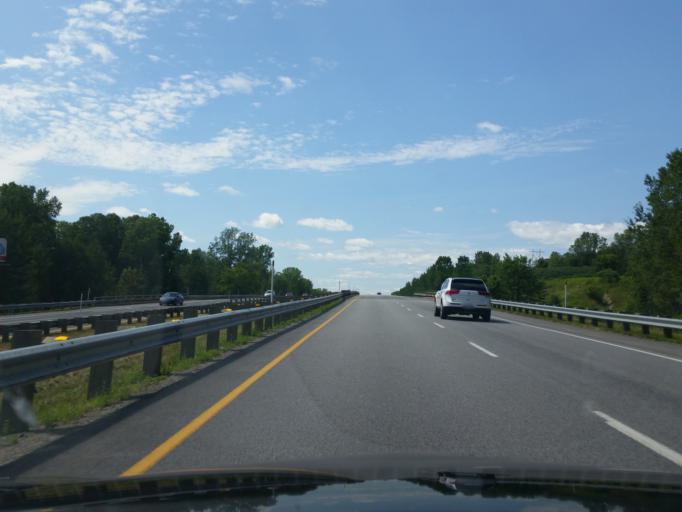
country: CA
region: Quebec
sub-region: Monteregie
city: Hudson
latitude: 45.4434
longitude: -74.1987
